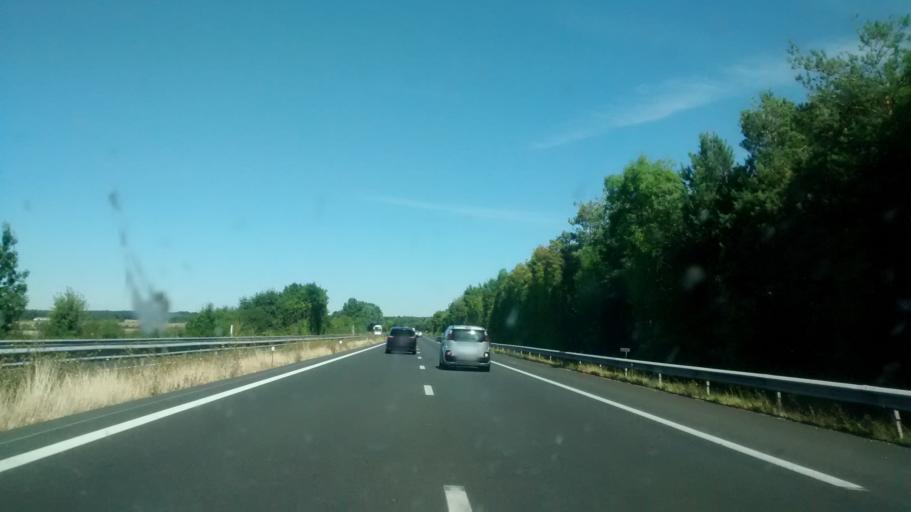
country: FR
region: Poitou-Charentes
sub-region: Departement de la Charente-Maritime
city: Saint-Jean-d'Angely
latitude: 46.0660
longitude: -0.5341
